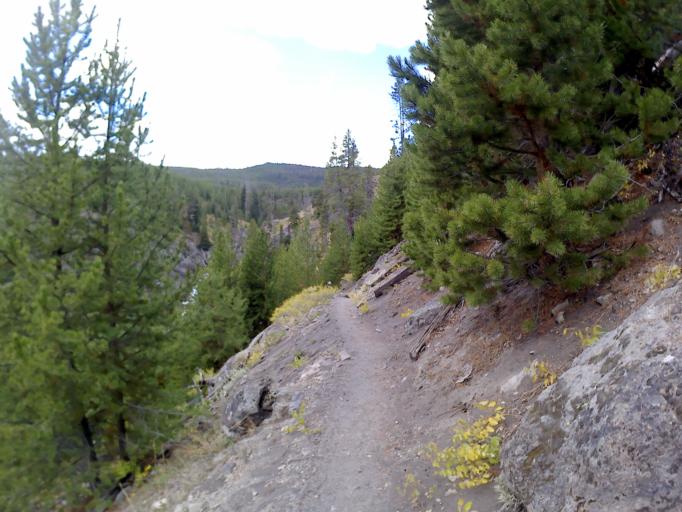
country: US
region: Montana
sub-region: Gallatin County
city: West Yellowstone
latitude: 44.4848
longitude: -110.8725
